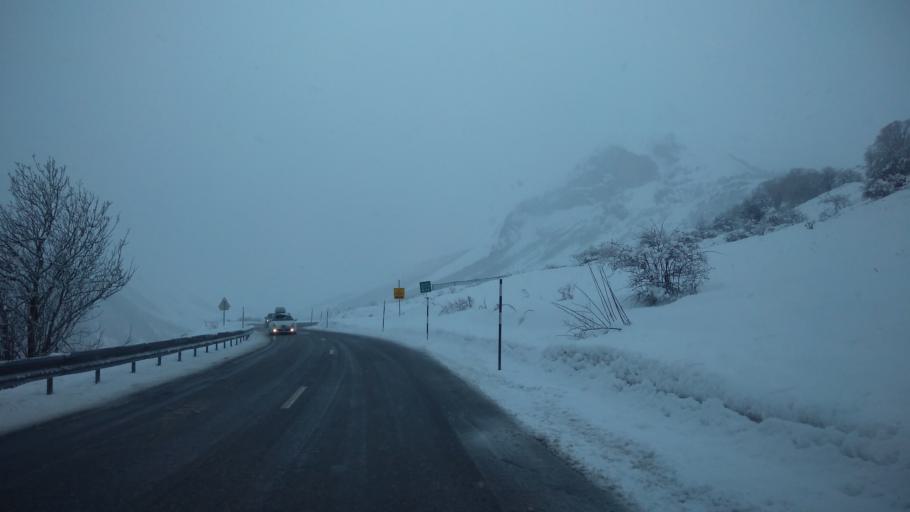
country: FR
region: Provence-Alpes-Cote d'Azur
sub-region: Departement des Hautes-Alpes
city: Le Monetier-les-Bains
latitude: 45.0122
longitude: 6.4689
